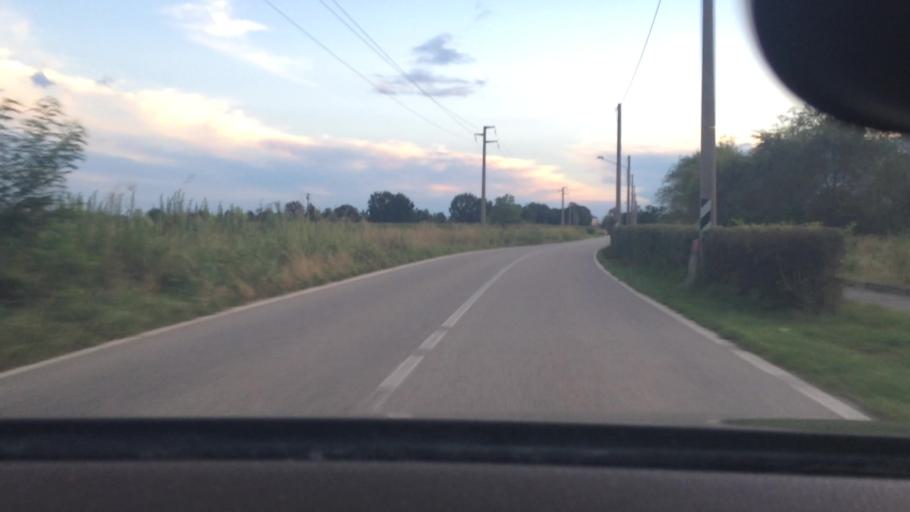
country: IT
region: Lombardy
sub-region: Citta metropolitana di Milano
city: Mantegazza
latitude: 45.5158
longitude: 8.9815
